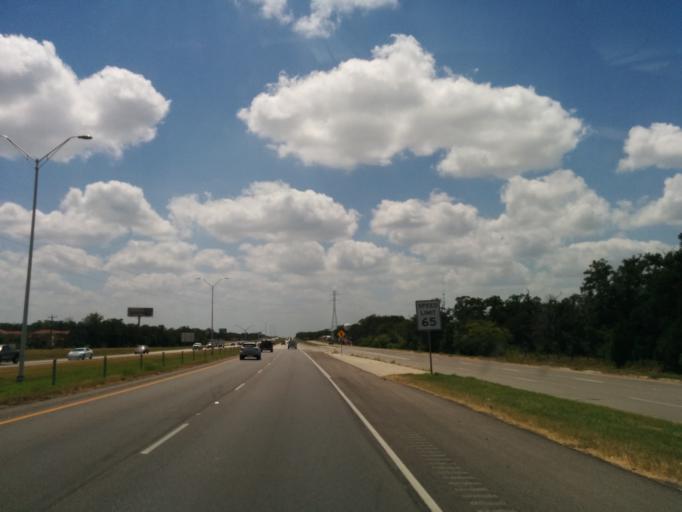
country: US
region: Texas
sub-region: Bastrop County
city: Bastrop
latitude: 30.1111
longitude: -97.3768
